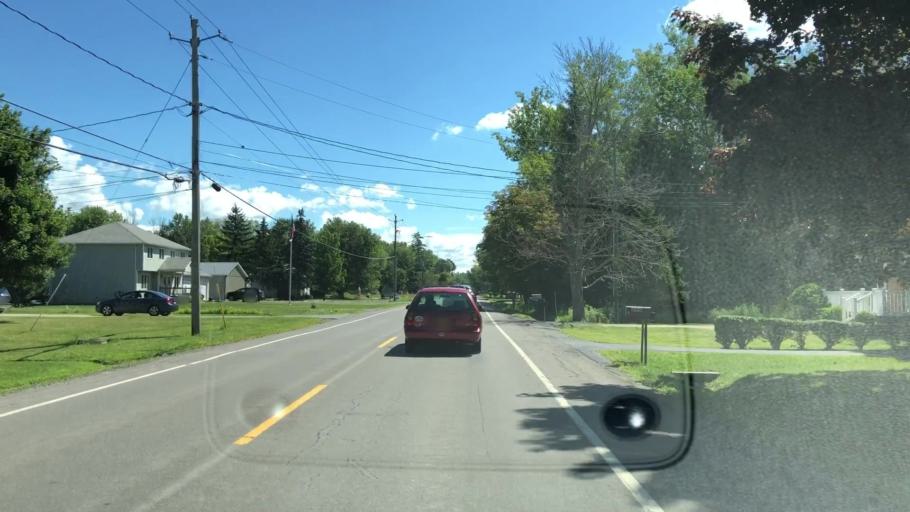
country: US
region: New York
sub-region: Erie County
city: Depew
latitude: 42.8509
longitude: -78.7210
